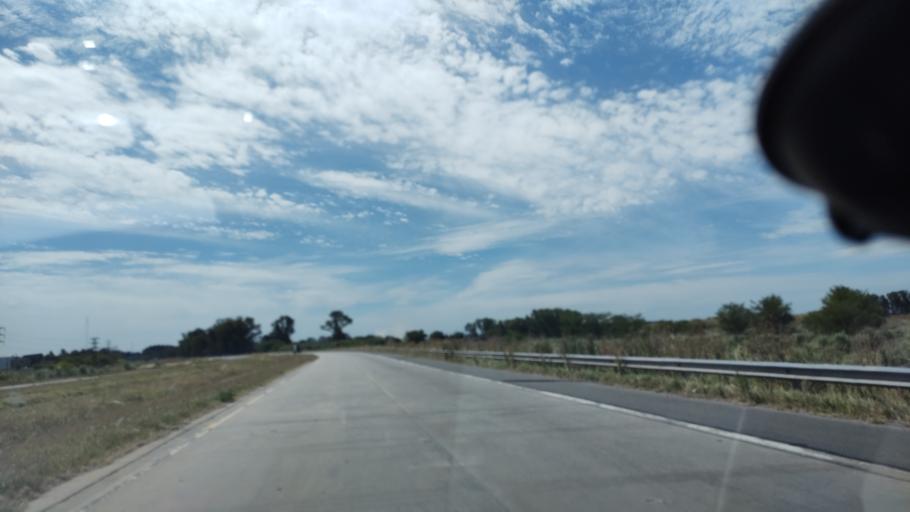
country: AR
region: Buenos Aires
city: Canuelas
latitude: -35.0415
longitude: -58.7132
